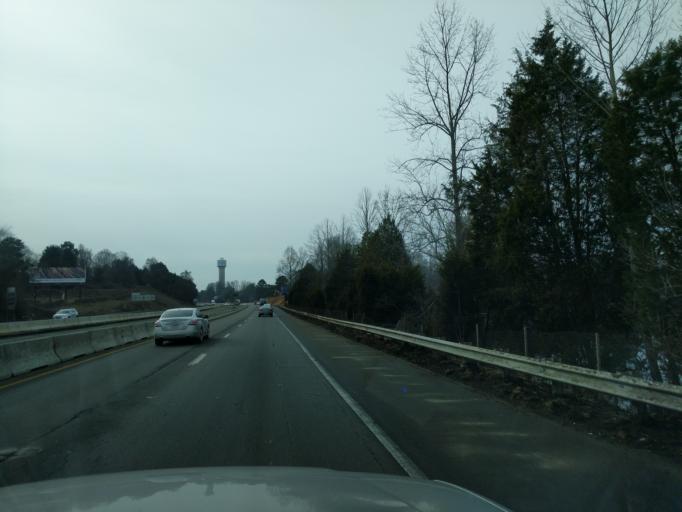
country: US
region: North Carolina
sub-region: Iredell County
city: Mooresville
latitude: 35.5668
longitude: -80.8579
